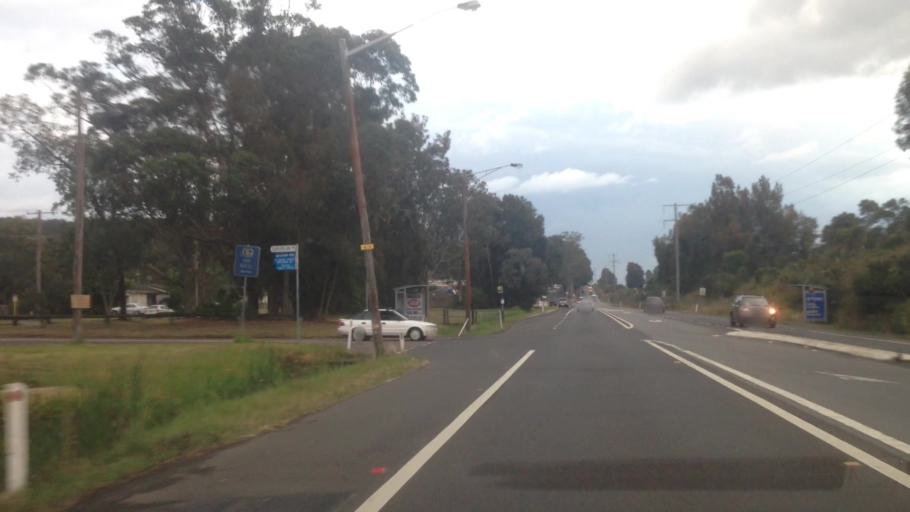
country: AU
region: New South Wales
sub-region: Wyong Shire
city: Chittaway Bay
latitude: -33.2769
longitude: 151.4284
